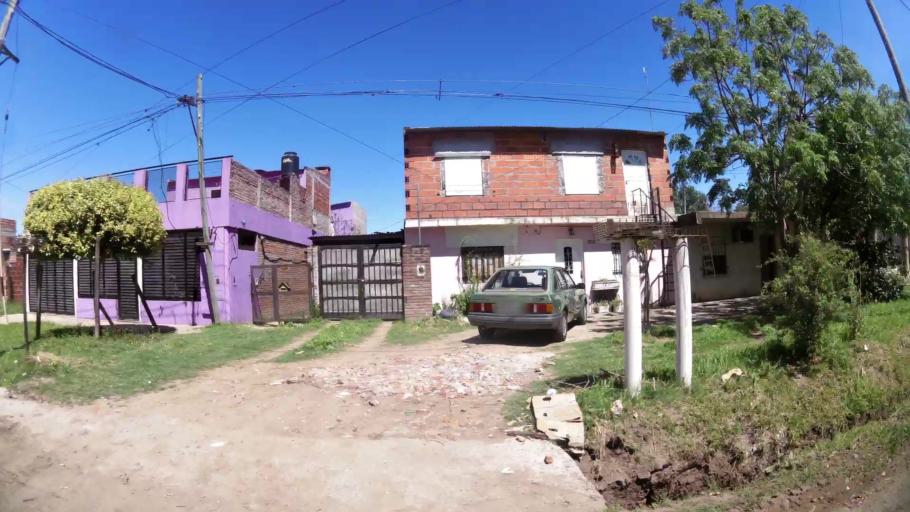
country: AR
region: Santa Fe
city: Perez
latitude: -32.9580
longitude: -60.7152
